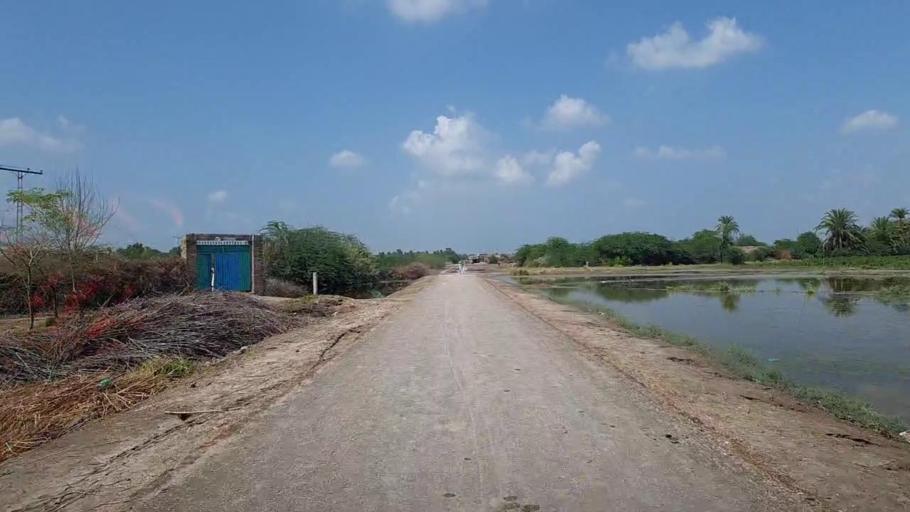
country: PK
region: Sindh
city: Kandiaro
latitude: 27.0286
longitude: 68.2768
